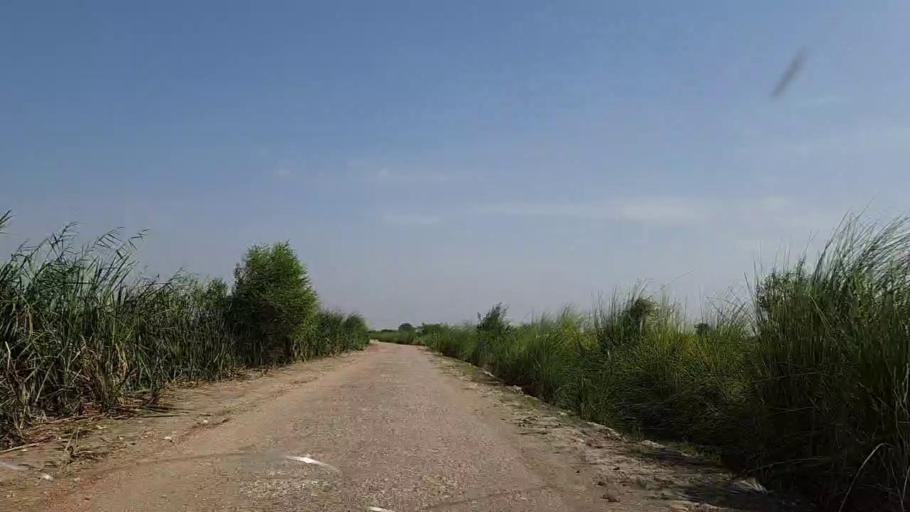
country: PK
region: Sindh
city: Khanpur
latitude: 27.7171
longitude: 69.3615
